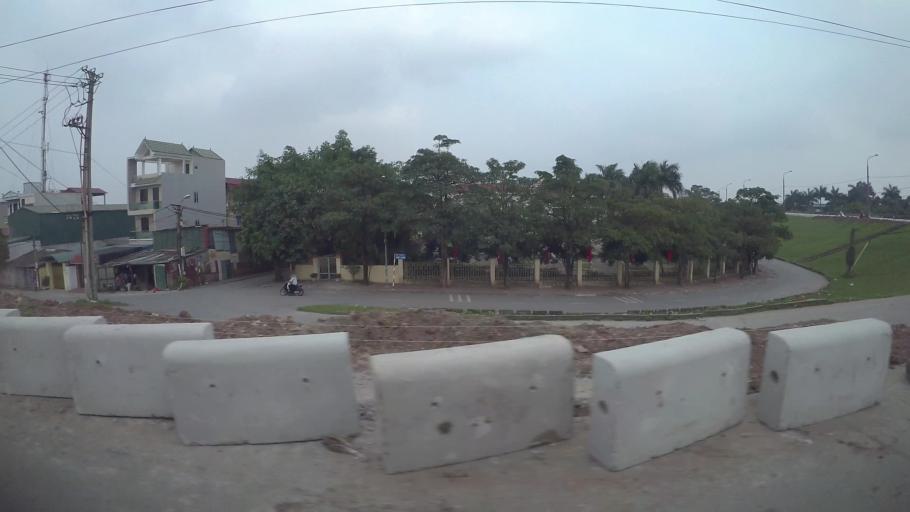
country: VN
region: Ha Noi
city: Trau Quy
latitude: 21.0121
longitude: 105.9041
